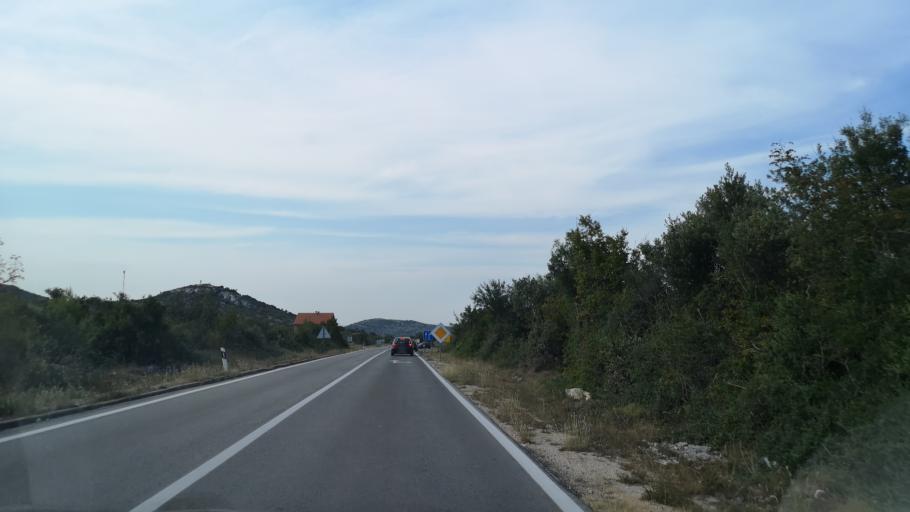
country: HR
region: Sibensko-Kniniska
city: Zaton
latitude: 43.8324
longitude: 15.7780
